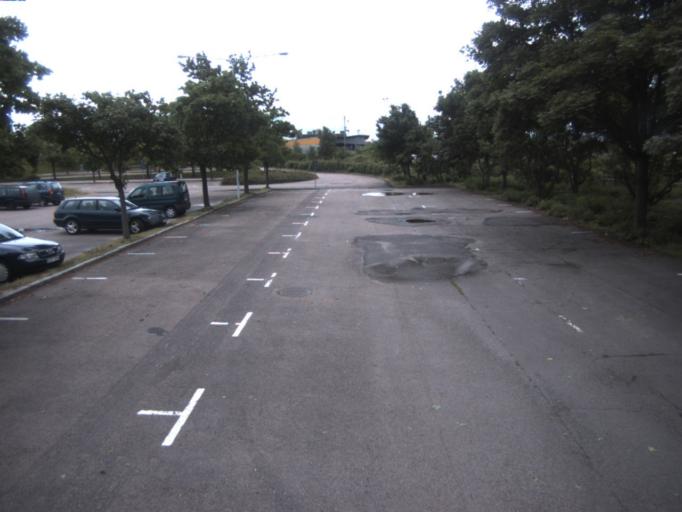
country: SE
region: Skane
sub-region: Helsingborg
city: Helsingborg
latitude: 56.0351
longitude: 12.7046
